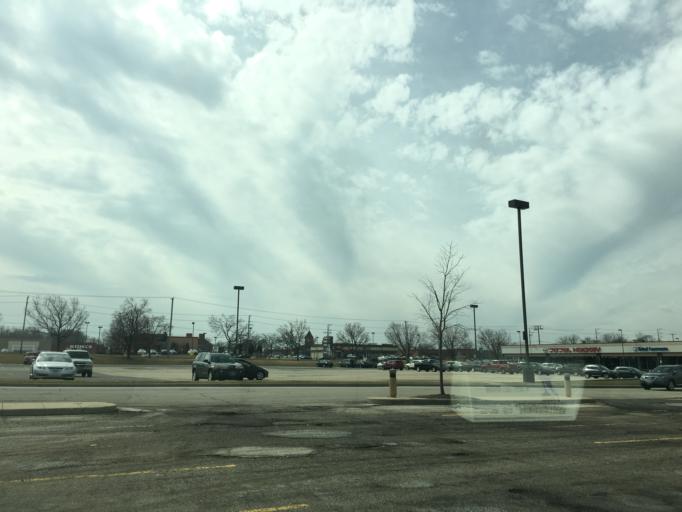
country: US
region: Illinois
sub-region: DuPage County
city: Woodridge
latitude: 41.7524
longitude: -88.0146
